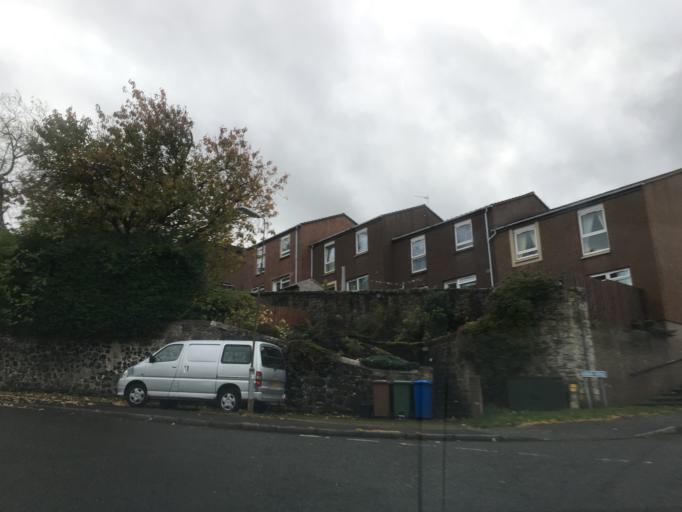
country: GB
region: Scotland
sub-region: Falkirk
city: Bo'ness
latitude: 56.0169
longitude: -3.6043
